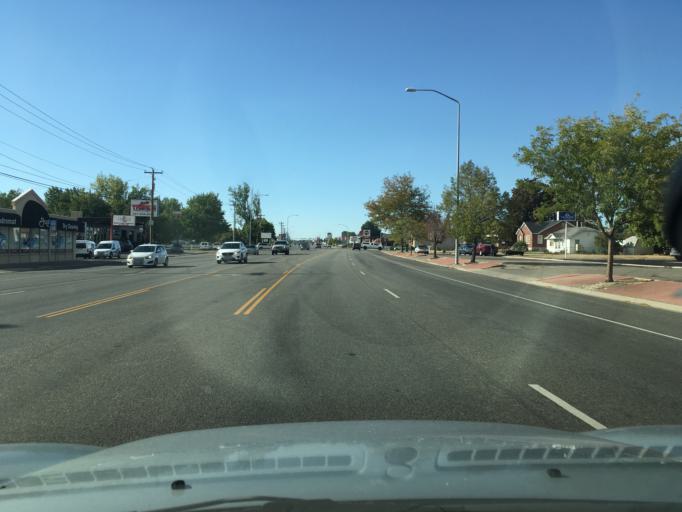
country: US
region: Utah
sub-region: Davis County
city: Layton
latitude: 41.0632
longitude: -111.9690
